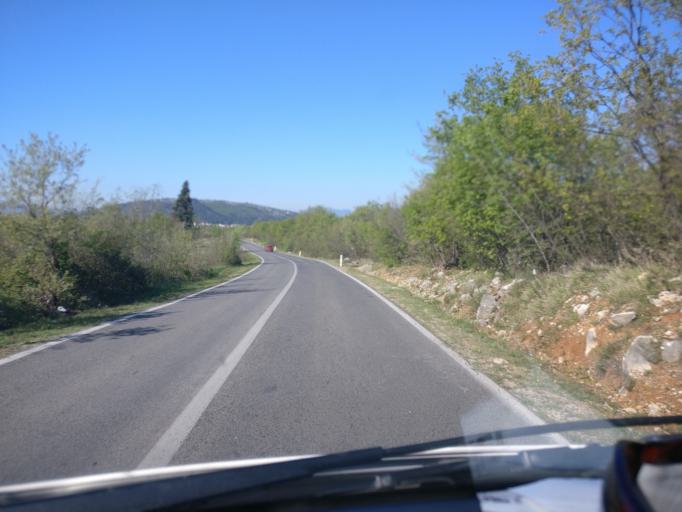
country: BA
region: Federation of Bosnia and Herzegovina
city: Tasovcici
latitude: 43.1308
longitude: 17.7677
